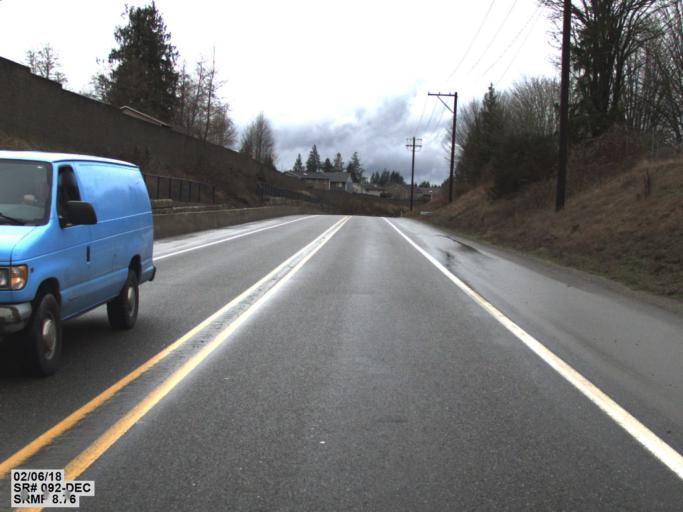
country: US
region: Washington
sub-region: Snohomish County
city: Granite Falls
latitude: 48.0914
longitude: -121.9693
